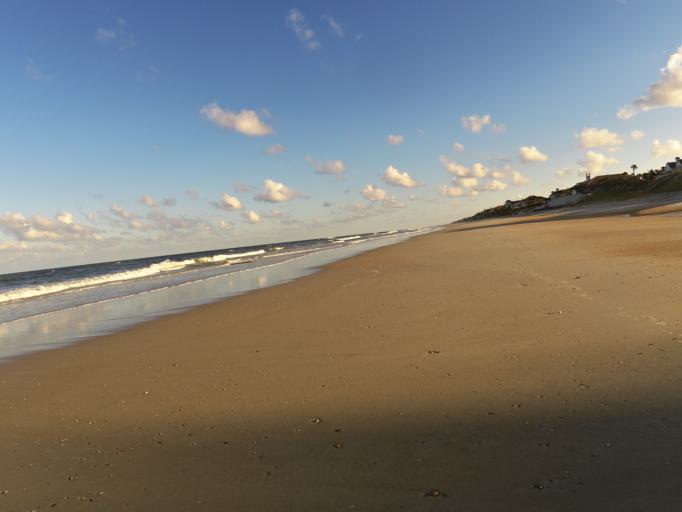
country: US
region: Florida
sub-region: Saint Johns County
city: Sawgrass
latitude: 30.1746
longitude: -81.3587
